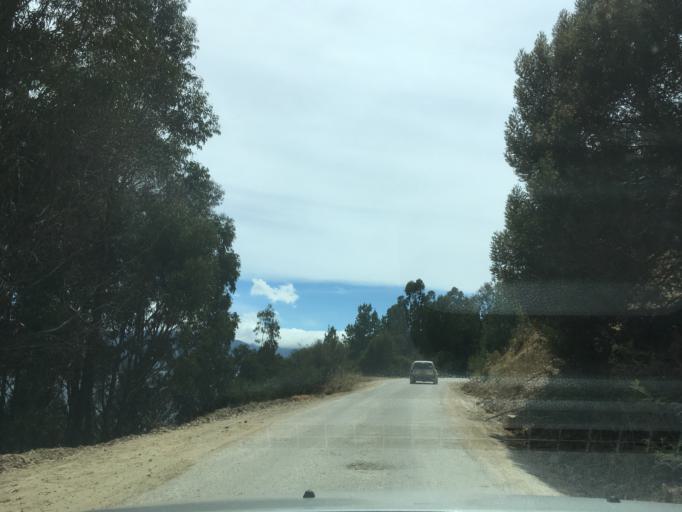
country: CO
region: Boyaca
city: Aquitania
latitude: 5.5881
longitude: -72.9211
